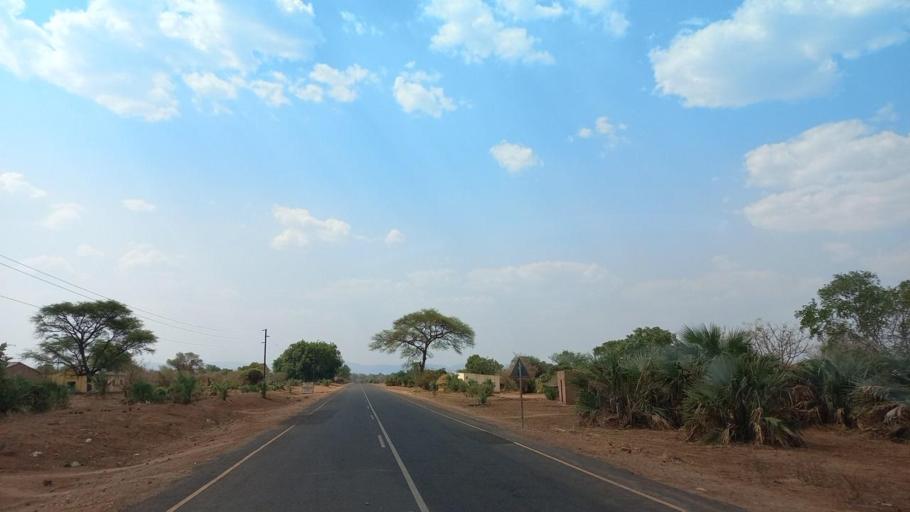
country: ZM
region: Lusaka
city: Luangwa
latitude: -15.1793
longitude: 30.2199
